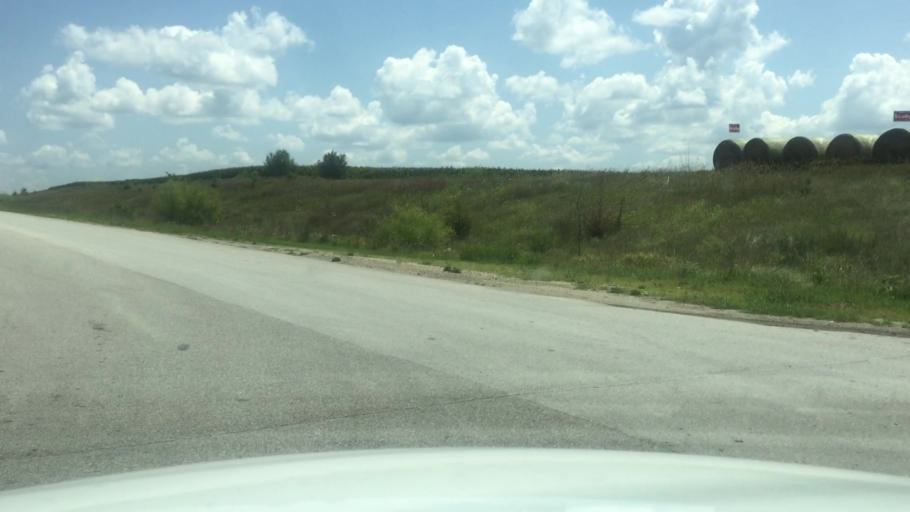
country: US
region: Kansas
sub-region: Nemaha County
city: Sabetha
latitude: 39.8852
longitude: -95.7882
